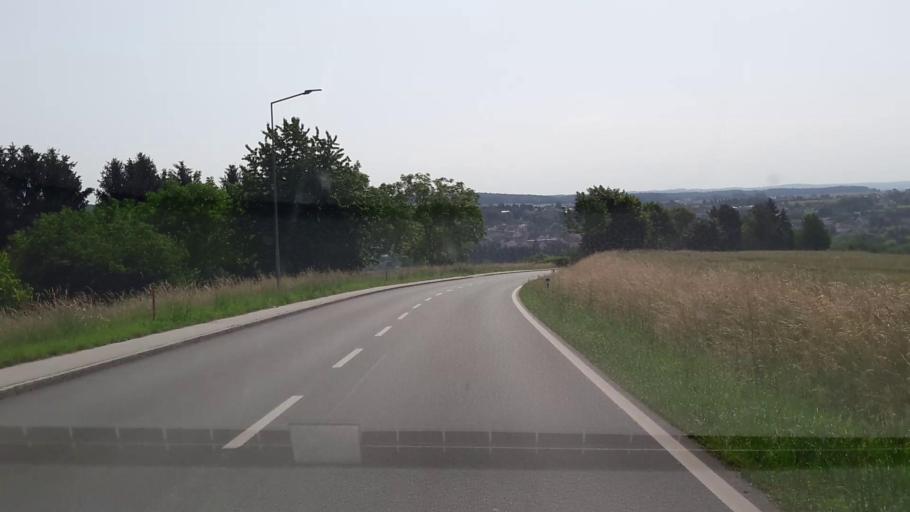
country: AT
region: Burgenland
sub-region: Politischer Bezirk Gussing
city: Stegersbach
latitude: 47.1618
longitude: 16.1530
